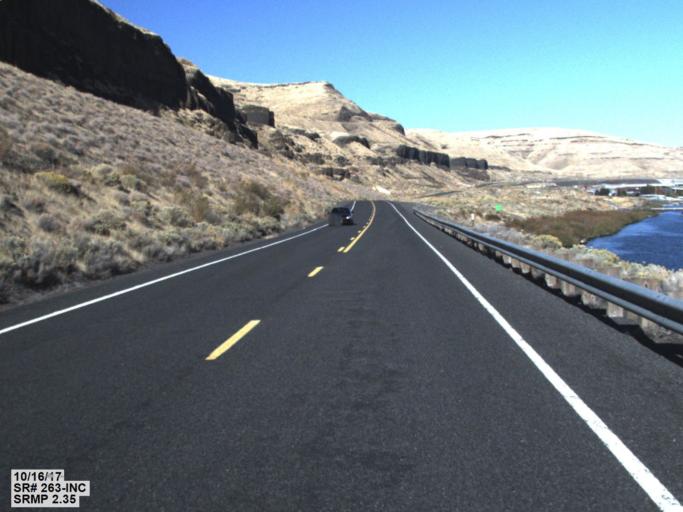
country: US
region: Washington
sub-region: Franklin County
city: Connell
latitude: 46.5544
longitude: -118.5522
